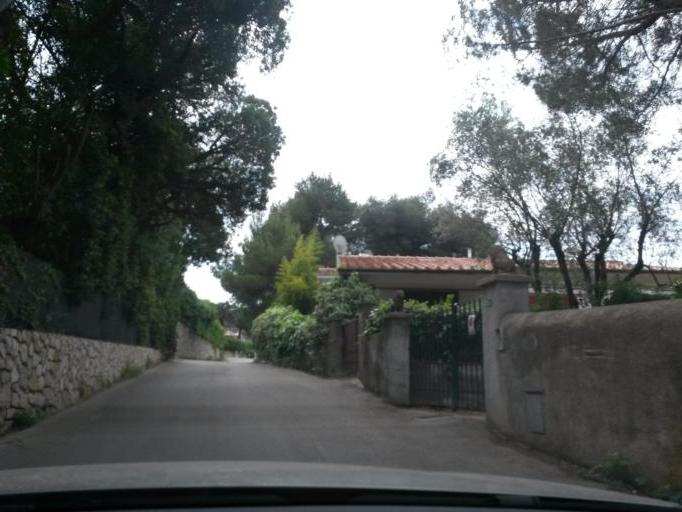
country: IT
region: Tuscany
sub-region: Provincia di Livorno
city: Rio nell'Elba
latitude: 42.7990
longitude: 10.3589
